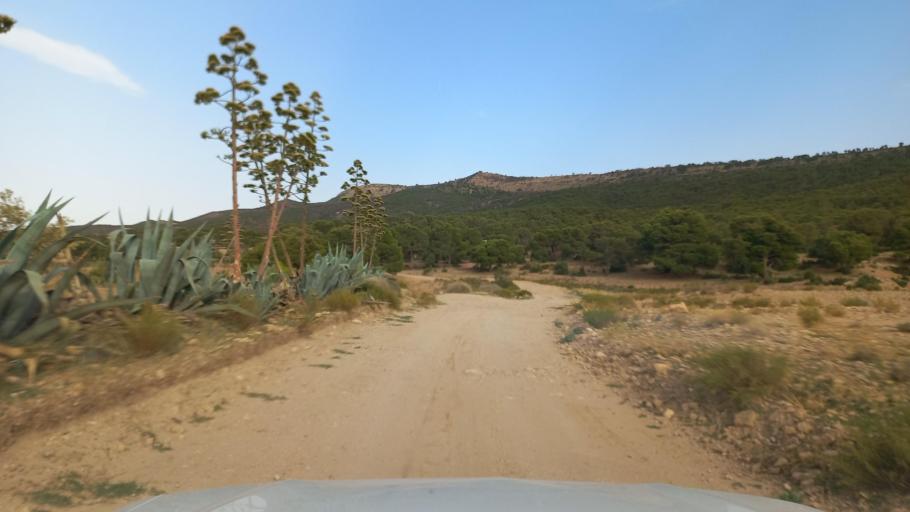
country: TN
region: Al Qasrayn
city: Kasserine
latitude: 35.3336
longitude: 8.8492
